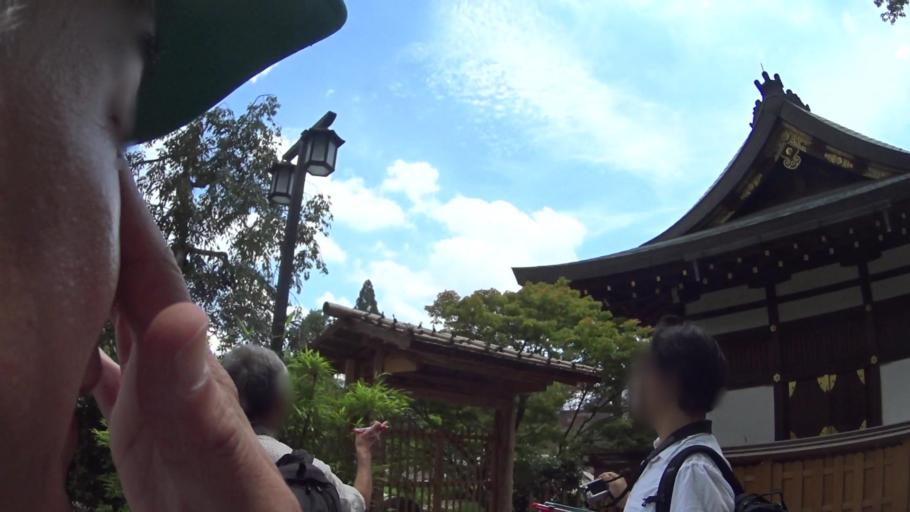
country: JP
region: Kyoto
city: Kyoto
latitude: 35.0308
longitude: 135.7346
